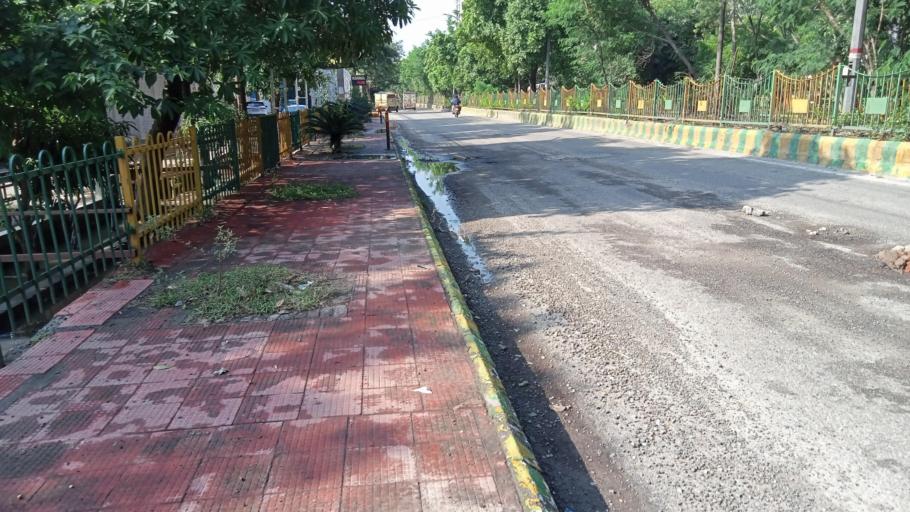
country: IN
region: Uttar Pradesh
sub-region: Ghaziabad
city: Ghaziabad
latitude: 28.6638
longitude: 77.3725
